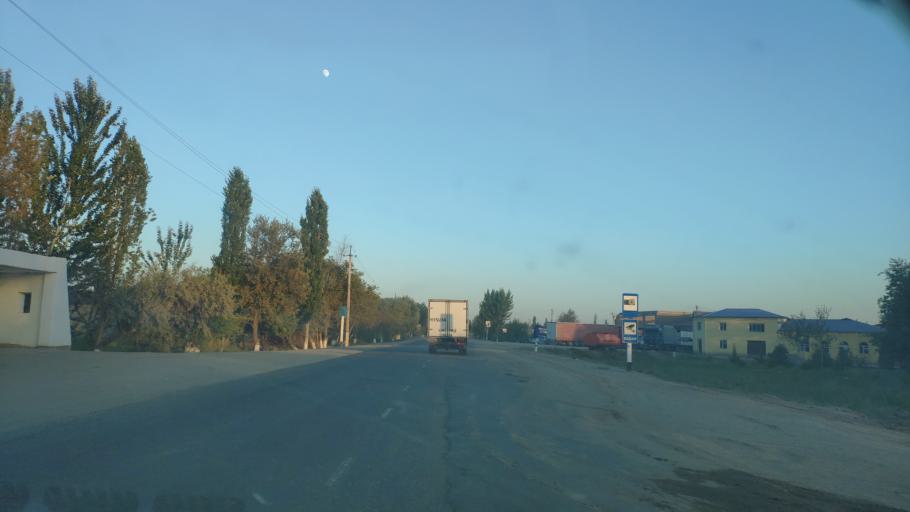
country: UZ
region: Karakalpakstan
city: To'rtko'l Shahri
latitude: 41.5668
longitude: 60.9521
